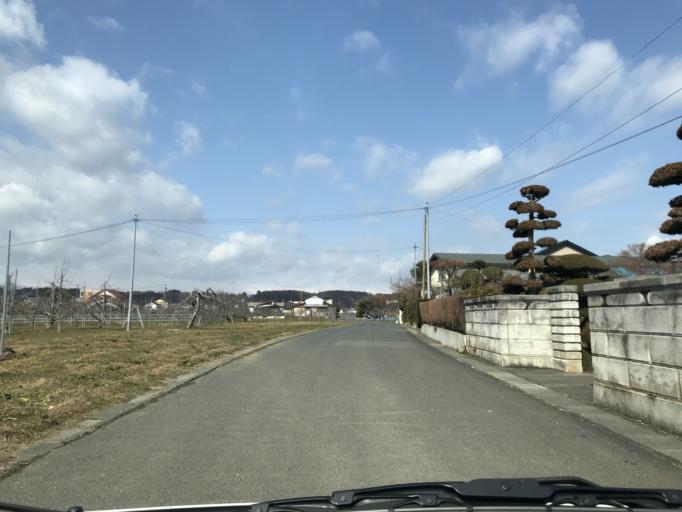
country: JP
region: Iwate
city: Mizusawa
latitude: 39.0441
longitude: 141.1401
